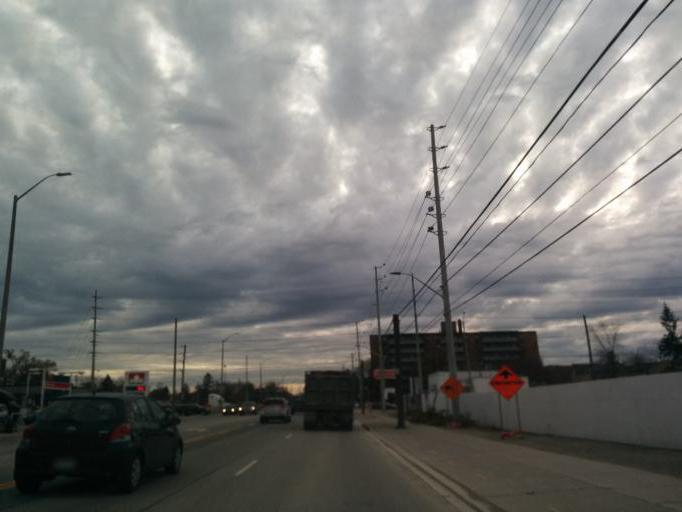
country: CA
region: Ontario
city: Mississauga
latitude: 43.5656
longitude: -79.5708
